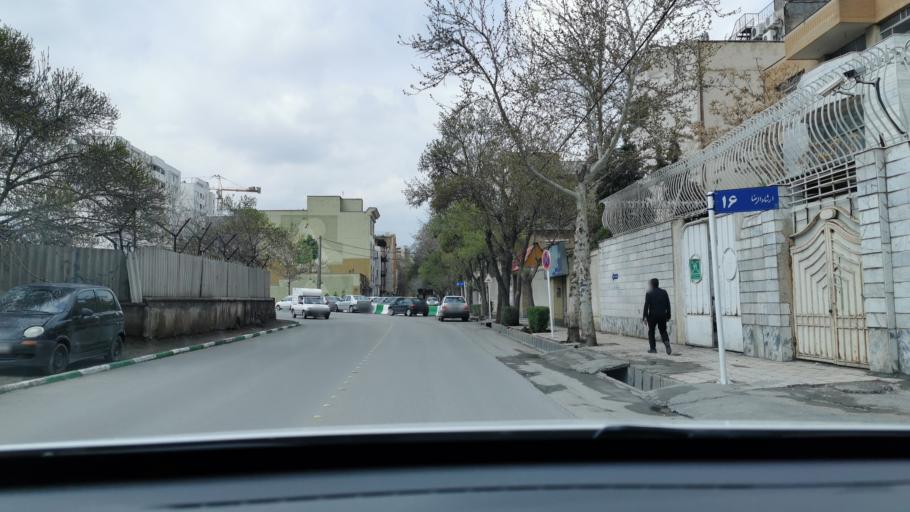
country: IR
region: Razavi Khorasan
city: Mashhad
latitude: 36.2852
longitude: 59.5902
